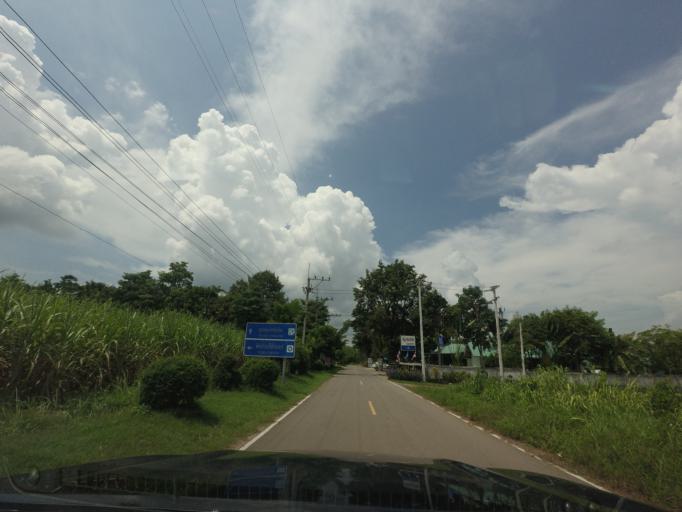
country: TH
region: Khon Kaen
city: Wiang Kao
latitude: 16.6792
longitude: 102.2685
